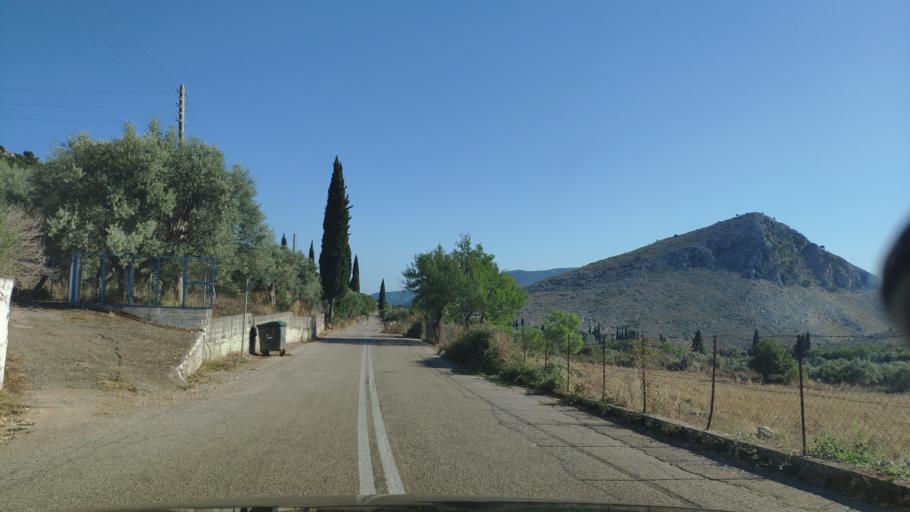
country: GR
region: West Greece
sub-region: Nomos Aitolias kai Akarnanias
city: Archontochorion
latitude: 38.6994
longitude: 21.0409
